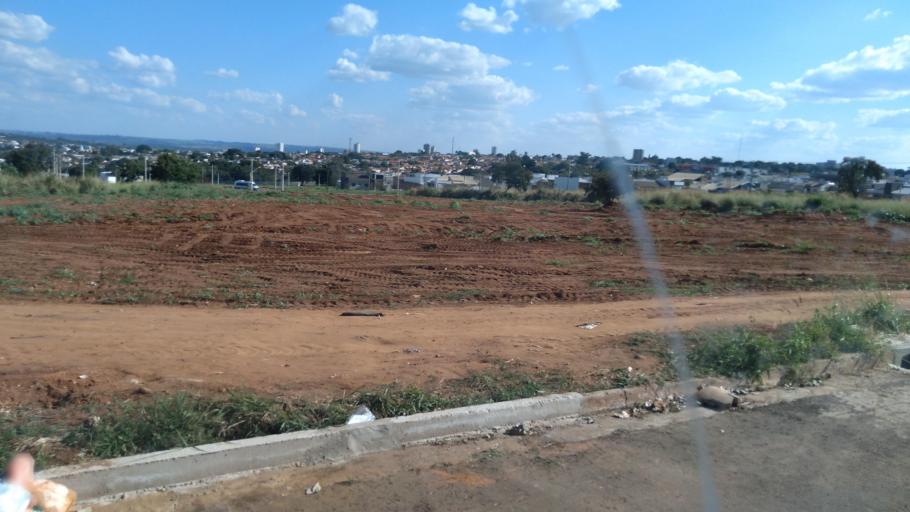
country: YE
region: Al Mahrah
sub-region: Shahan
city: Shihan as Sufla
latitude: 17.5514
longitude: 52.5393
